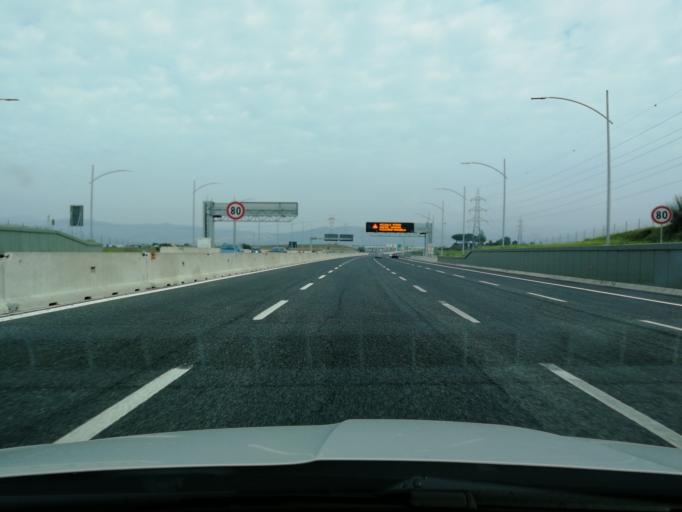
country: IT
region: Latium
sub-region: Citta metropolitana di Roma Capitale
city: Albuccione
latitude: 41.9254
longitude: 12.6935
